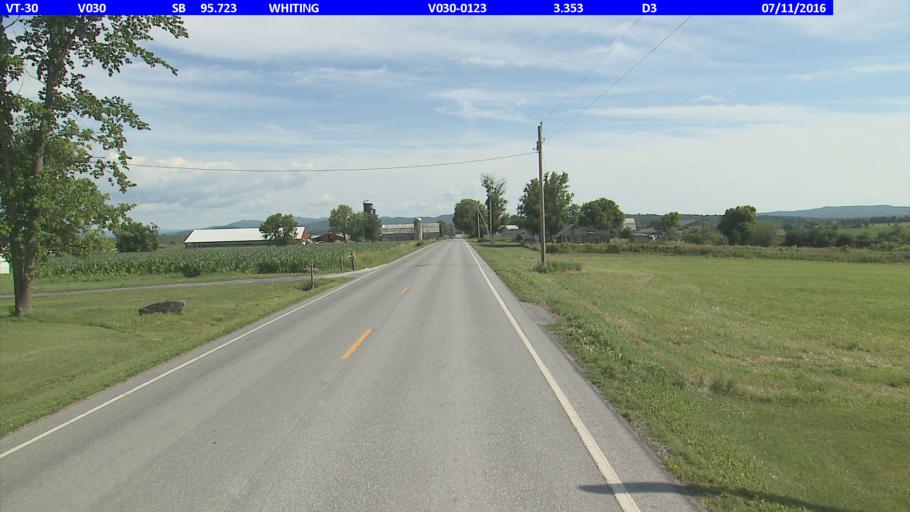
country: US
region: Vermont
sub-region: Addison County
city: Middlebury (village)
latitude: 43.8857
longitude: -73.2012
